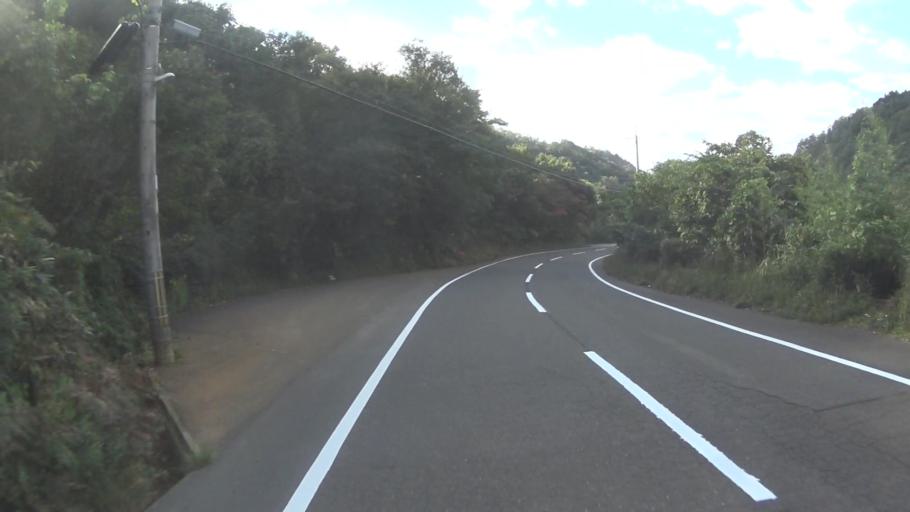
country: JP
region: Kyoto
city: Maizuru
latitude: 35.5543
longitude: 135.4439
